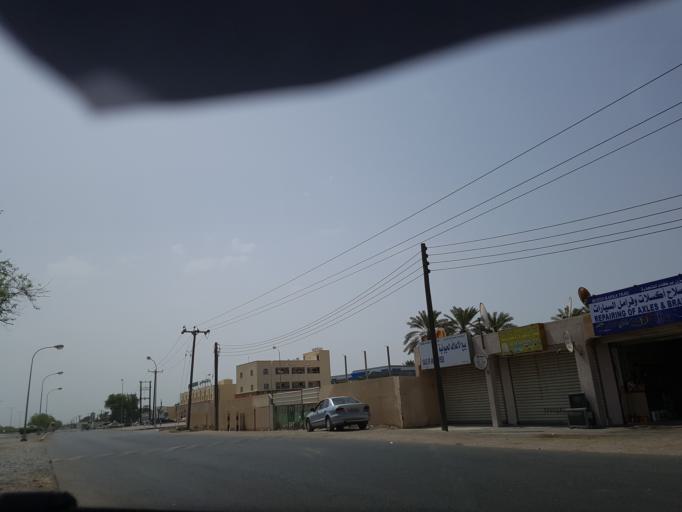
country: OM
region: Al Batinah
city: Barka'
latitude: 23.7131
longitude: 57.7498
